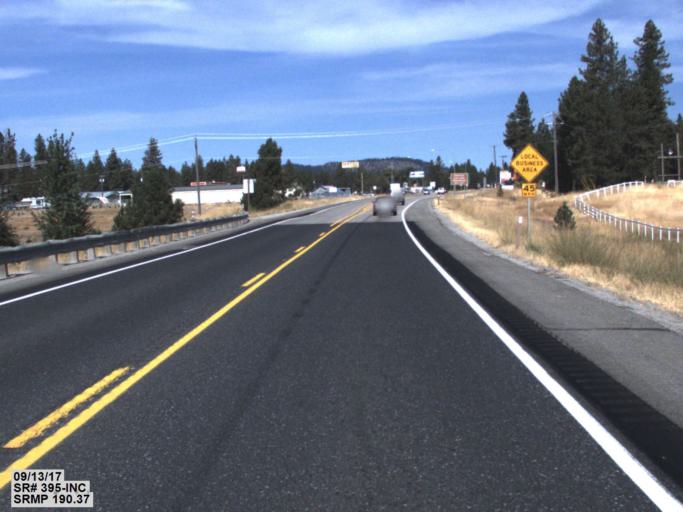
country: US
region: Washington
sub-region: Spokane County
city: Deer Park
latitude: 48.0572
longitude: -117.6186
